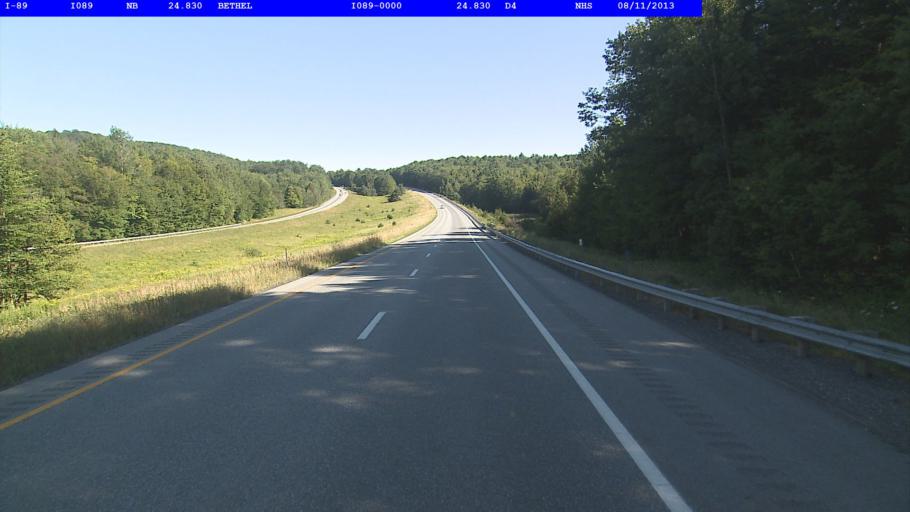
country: US
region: Vermont
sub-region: Orange County
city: Randolph
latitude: 43.8589
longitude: -72.6069
